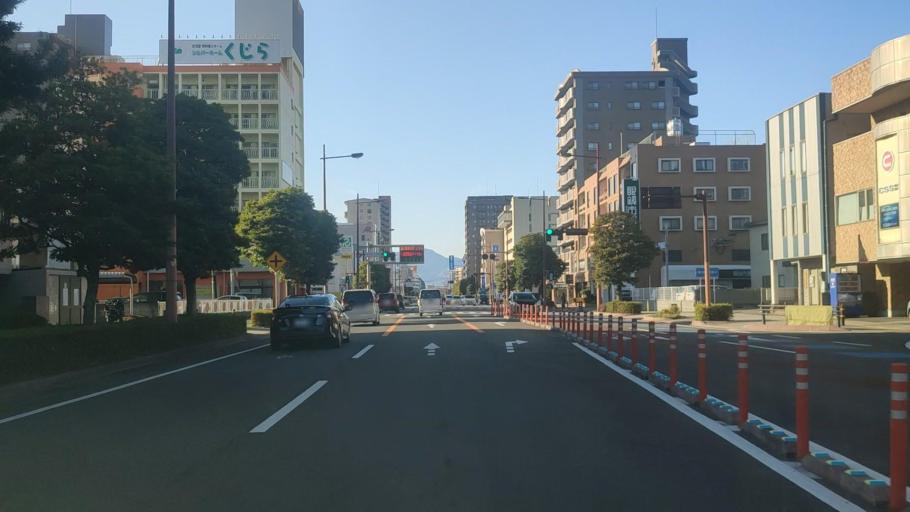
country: JP
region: Oita
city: Oita
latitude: 33.2398
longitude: 131.5962
